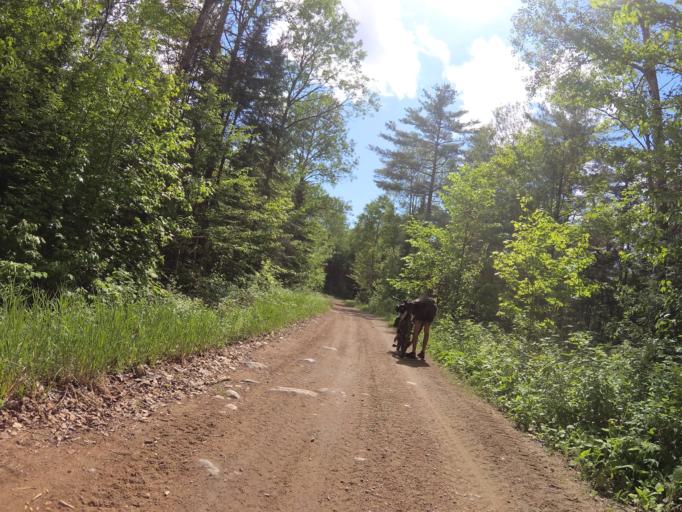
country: CA
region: Ontario
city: Renfrew
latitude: 45.1140
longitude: -76.8626
